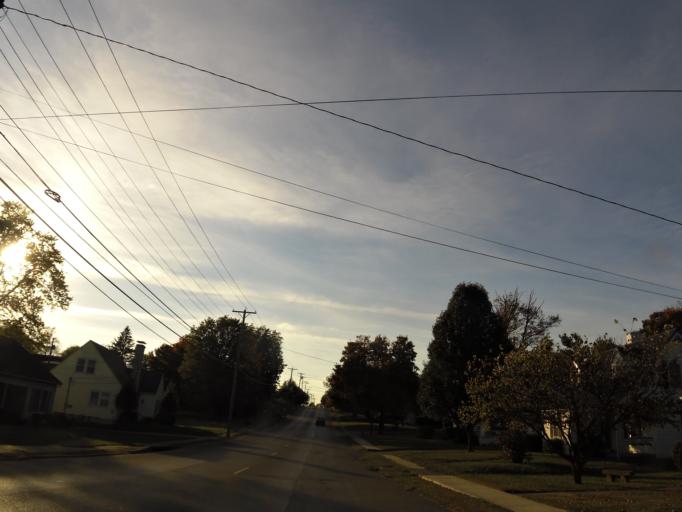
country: US
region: Kentucky
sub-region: Garrard County
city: Lancaster
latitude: 37.6199
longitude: -84.5841
